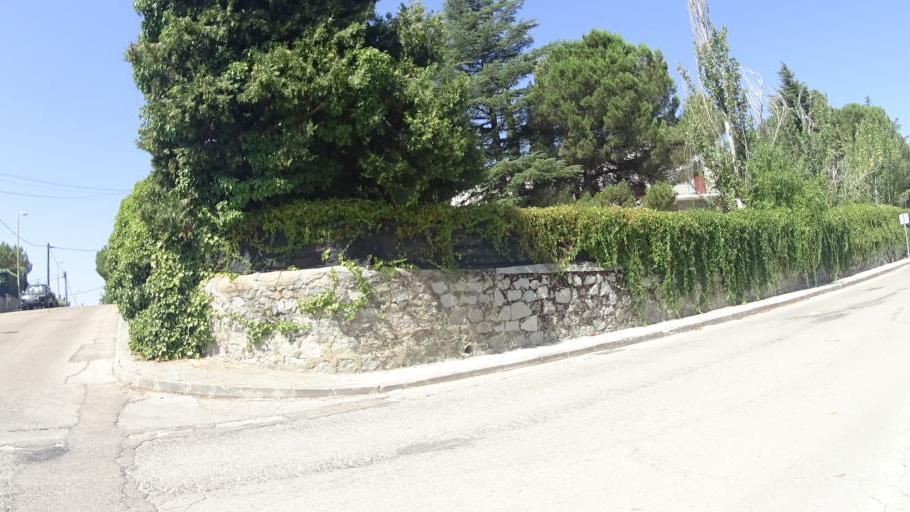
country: ES
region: Madrid
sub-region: Provincia de Madrid
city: Colmenarejo
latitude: 40.5584
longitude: -4.0089
